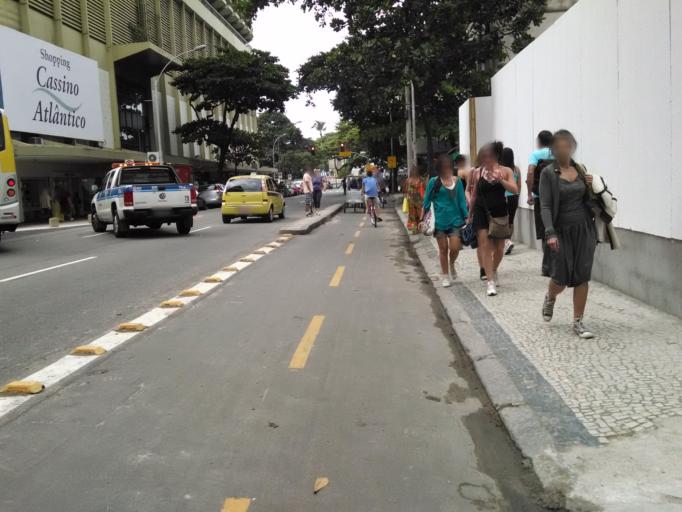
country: BR
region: Rio de Janeiro
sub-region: Rio De Janeiro
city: Rio de Janeiro
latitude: -22.9868
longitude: -43.1899
